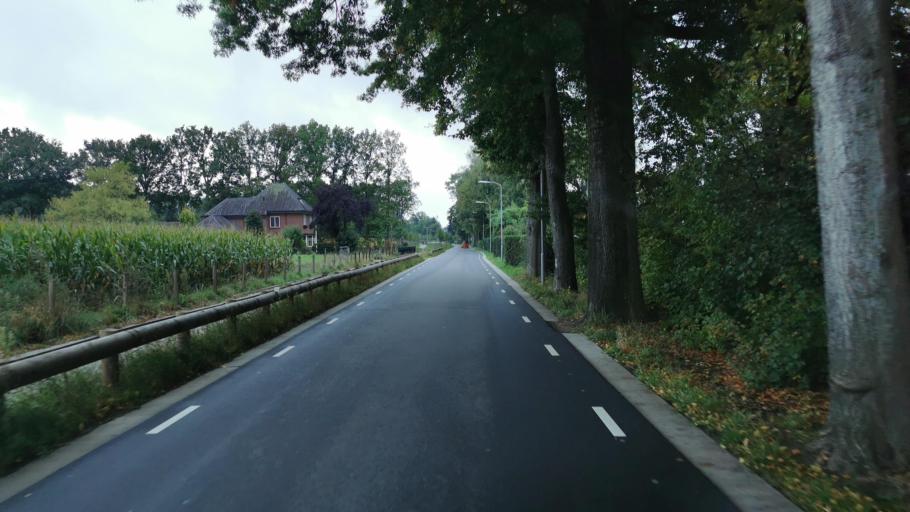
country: NL
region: Gelderland
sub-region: Gemeente Winterswijk
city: Winterswijk
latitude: 51.9736
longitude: 6.7398
